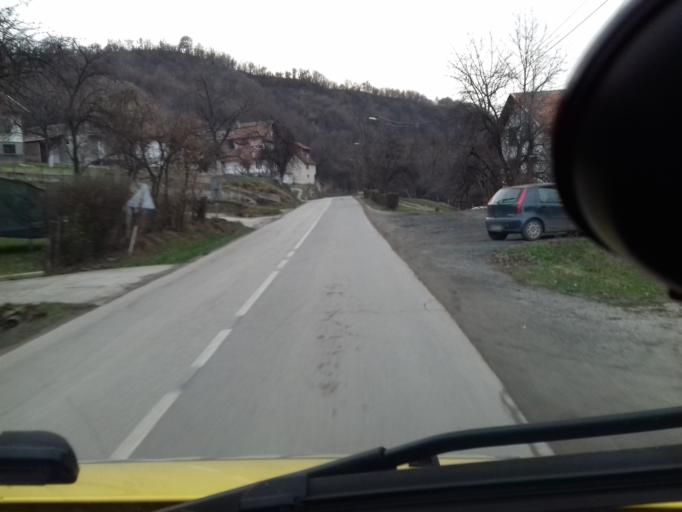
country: BA
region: Federation of Bosnia and Herzegovina
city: Zenica
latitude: 44.1873
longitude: 17.9435
